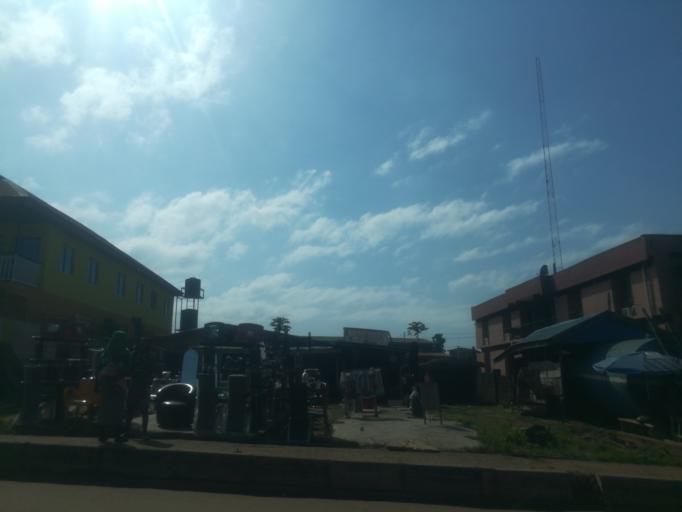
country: NG
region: Oyo
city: Ibadan
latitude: 7.4111
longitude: 3.9519
